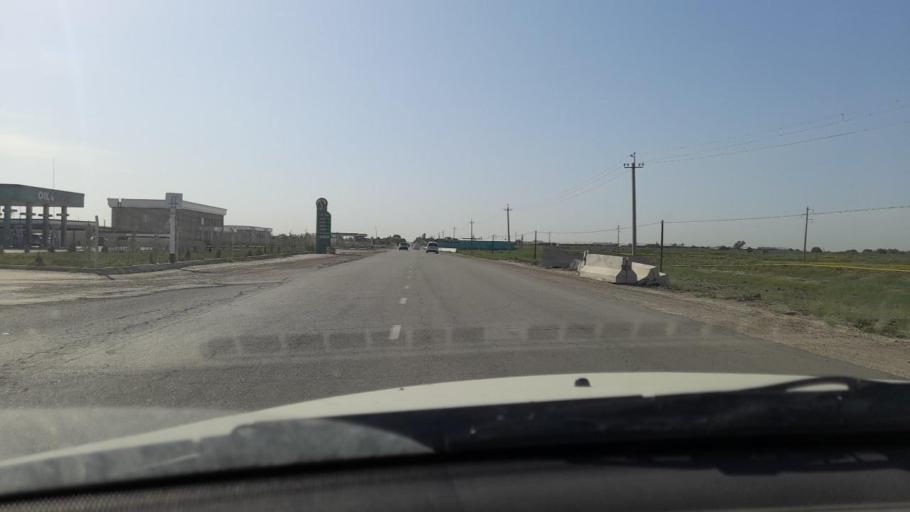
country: UZ
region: Bukhara
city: Romiton
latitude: 39.9162
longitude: 64.3899
